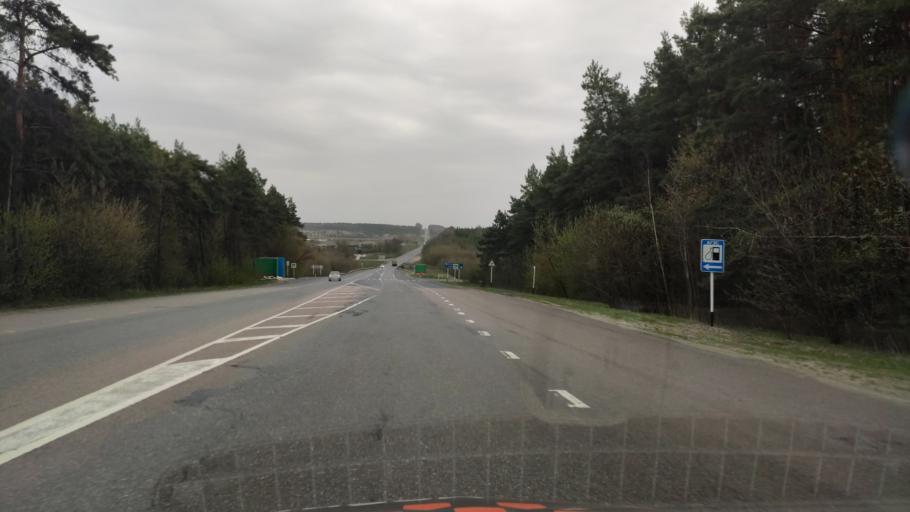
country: RU
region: Kursk
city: Gorshechnoye
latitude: 51.4665
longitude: 37.9310
